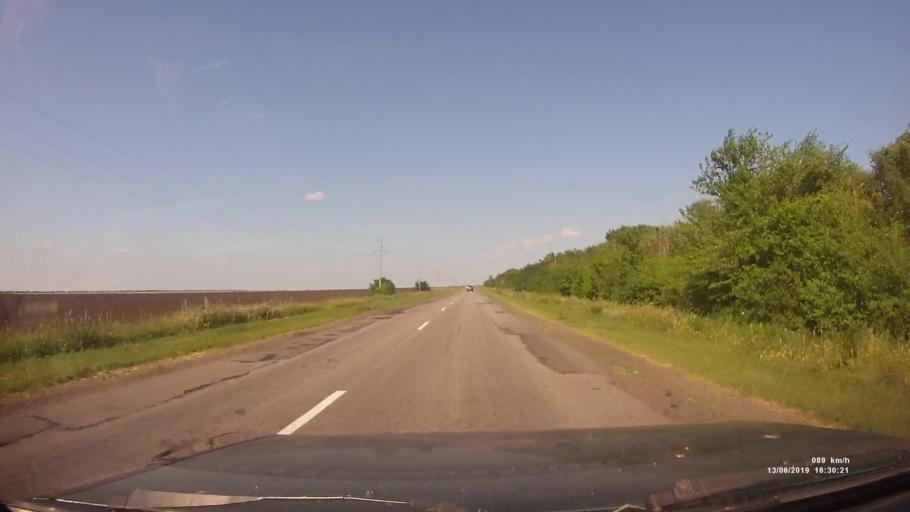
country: RU
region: Rostov
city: Kazanskaya
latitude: 49.8375
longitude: 41.2328
